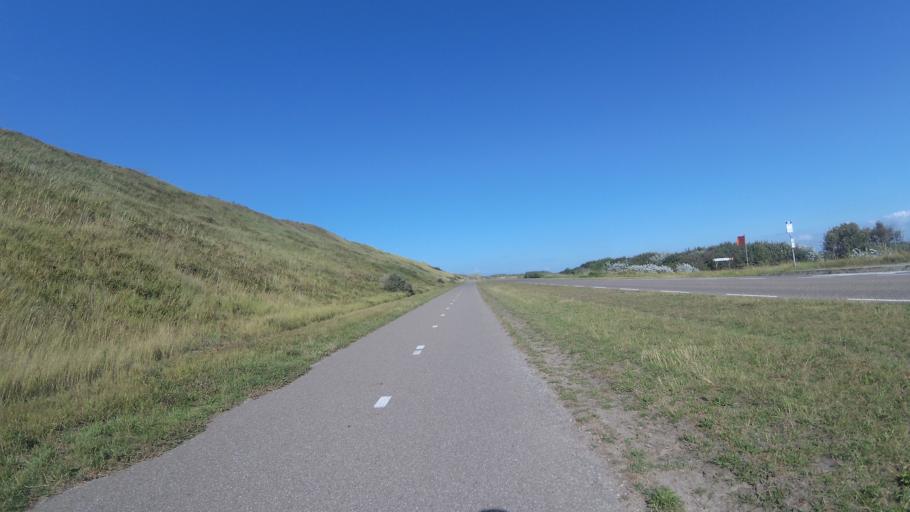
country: NL
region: Zeeland
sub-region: Gemeente Vlissingen
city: Vlissingen
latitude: 51.5438
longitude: 3.4452
